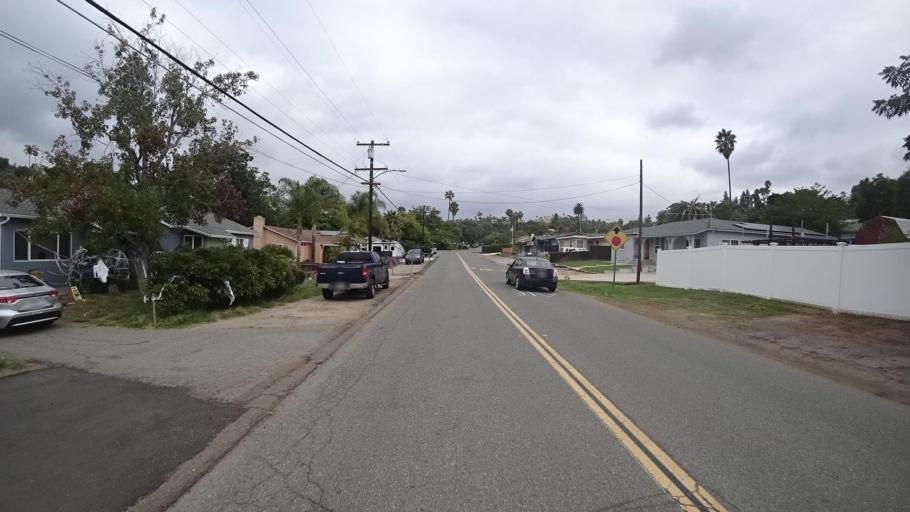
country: US
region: California
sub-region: San Diego County
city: Spring Valley
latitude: 32.7538
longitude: -116.9993
